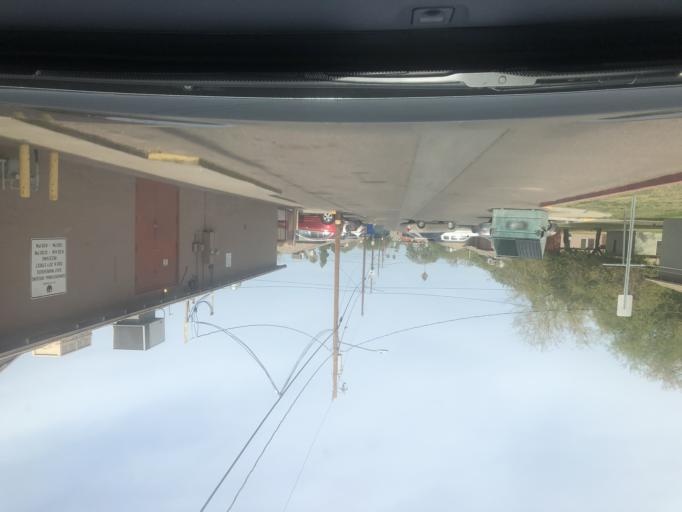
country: US
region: Arizona
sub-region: Maricopa County
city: Phoenix
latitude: 33.4536
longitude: -112.0402
